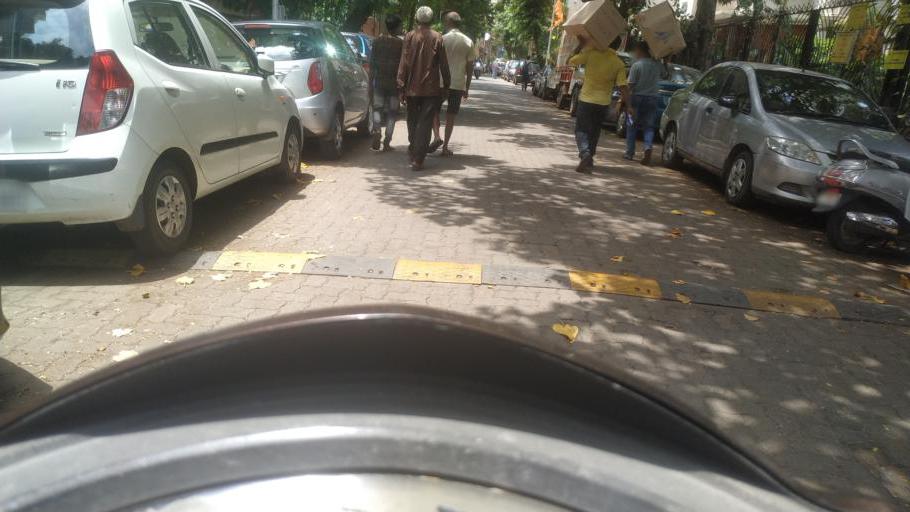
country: IN
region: Maharashtra
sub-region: Mumbai Suburban
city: Mumbai
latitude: 19.0175
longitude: 72.8368
